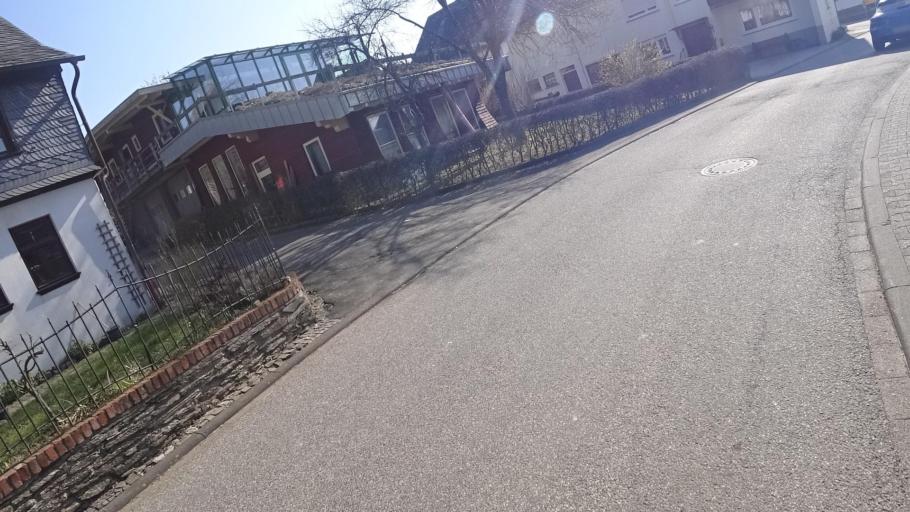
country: DE
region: Rheinland-Pfalz
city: Steinbach
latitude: 50.0439
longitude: 7.5946
